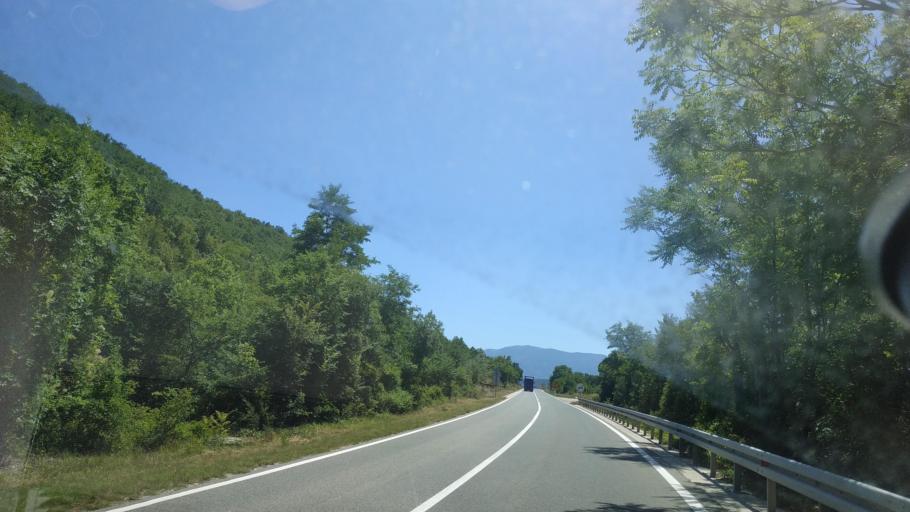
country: HR
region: Sibensko-Kniniska
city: Knin
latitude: 44.0327
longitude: 16.2250
